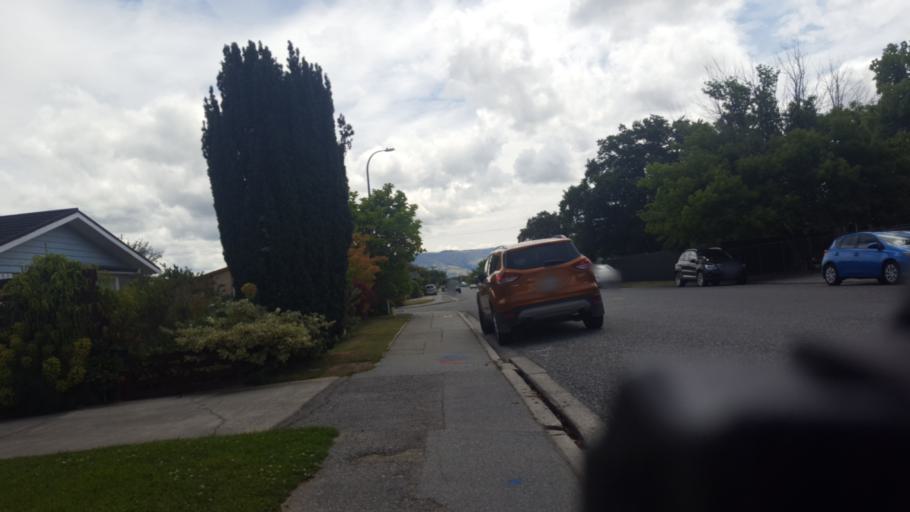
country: NZ
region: Otago
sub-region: Queenstown-Lakes District
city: Wanaka
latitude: -45.2556
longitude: 169.3887
